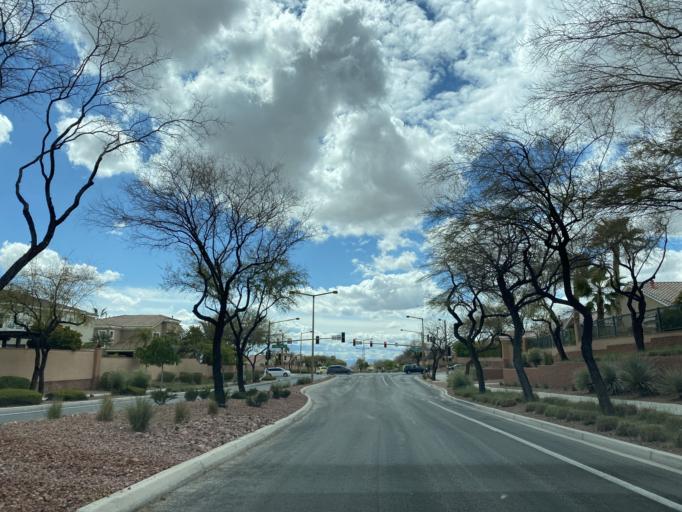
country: US
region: Nevada
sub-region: Clark County
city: Summerlin South
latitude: 36.1836
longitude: -115.3385
